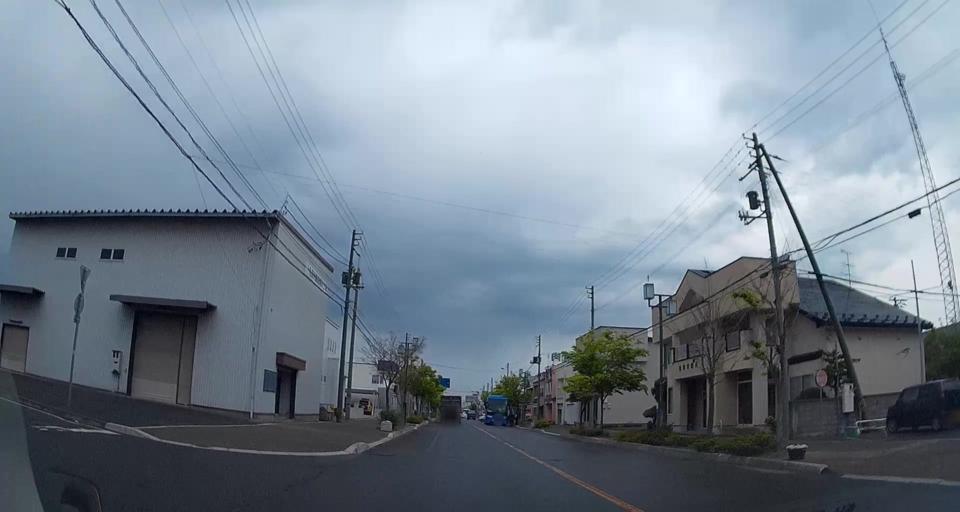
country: JP
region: Hokkaido
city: Chitose
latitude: 42.7265
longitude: 141.8800
